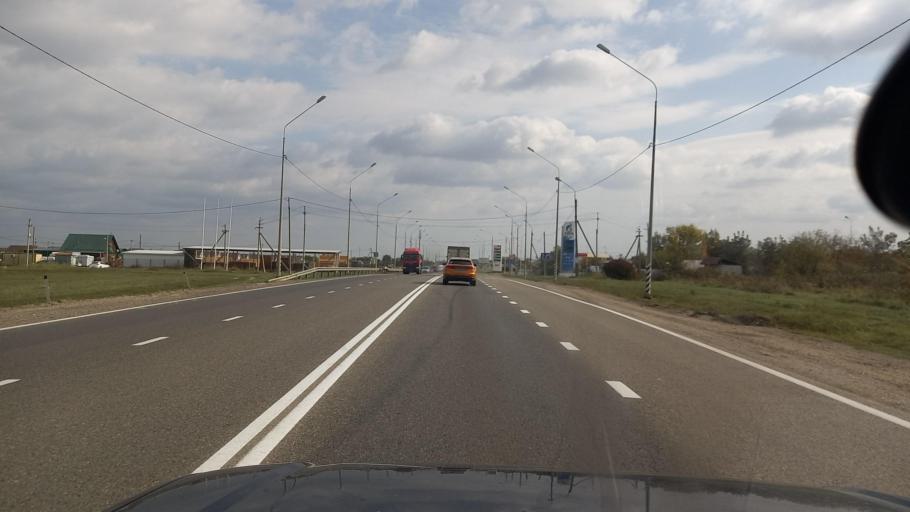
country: RU
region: Krasnodarskiy
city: Il'skiy
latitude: 44.8463
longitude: 38.5475
